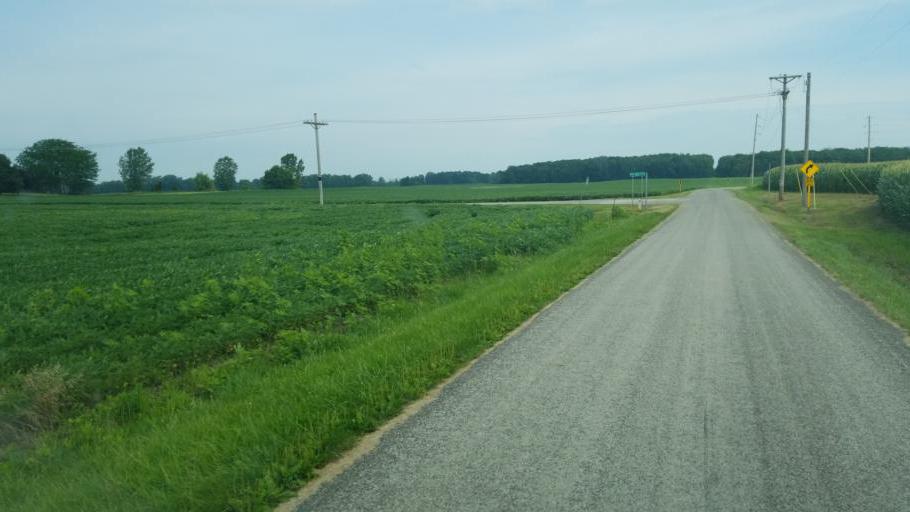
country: US
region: Ohio
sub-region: Wyandot County
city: Upper Sandusky
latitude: 40.6573
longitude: -83.3048
